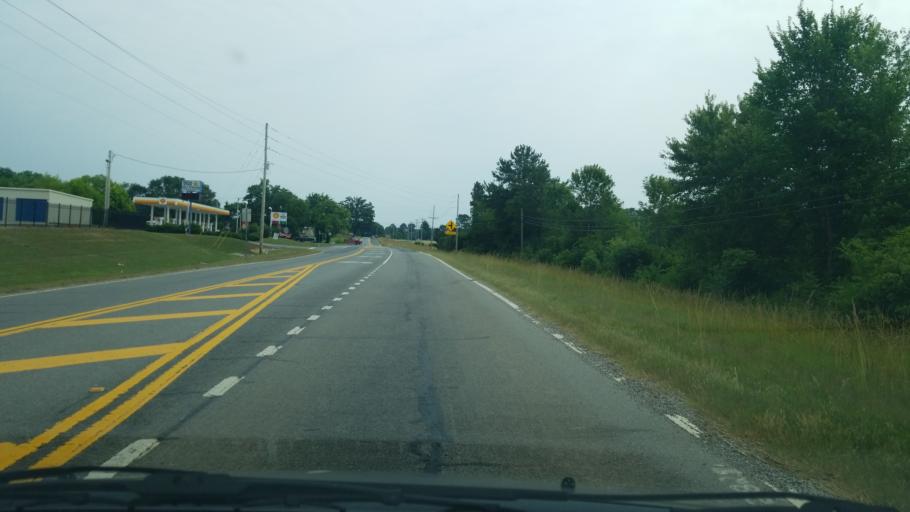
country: US
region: Georgia
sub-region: Catoosa County
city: Ringgold
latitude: 34.8691
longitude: -85.1425
